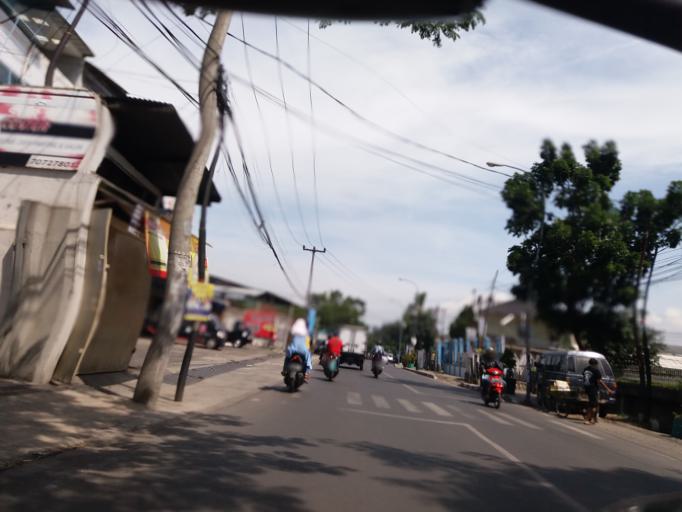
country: ID
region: West Java
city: Margahayukencana
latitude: -6.9407
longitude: 107.5680
